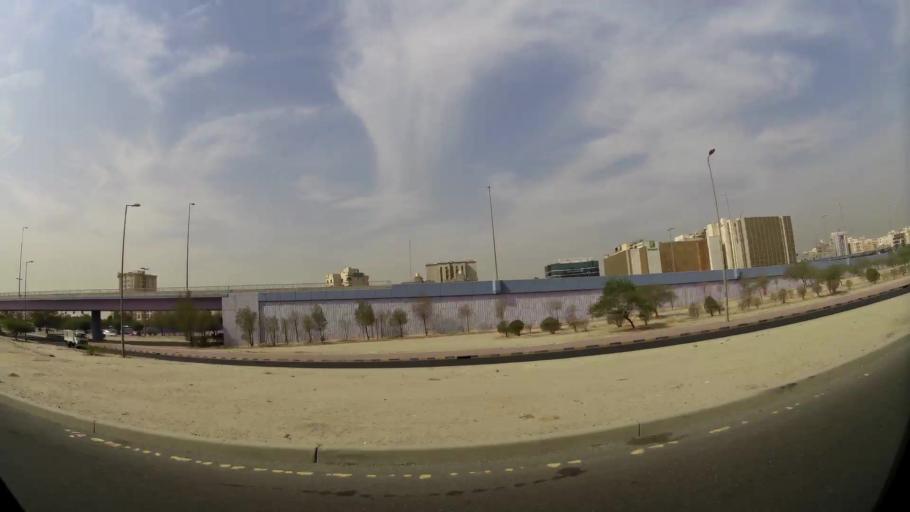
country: KW
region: Al Farwaniyah
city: Janub as Surrah
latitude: 29.2696
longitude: 47.9709
